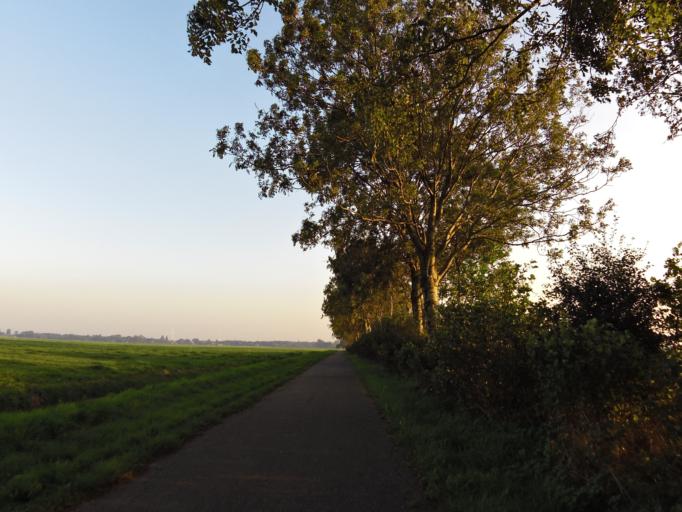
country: NL
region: South Holland
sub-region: Gemeente Leiderdorp
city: Leiderdorp
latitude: 52.1476
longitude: 4.5850
